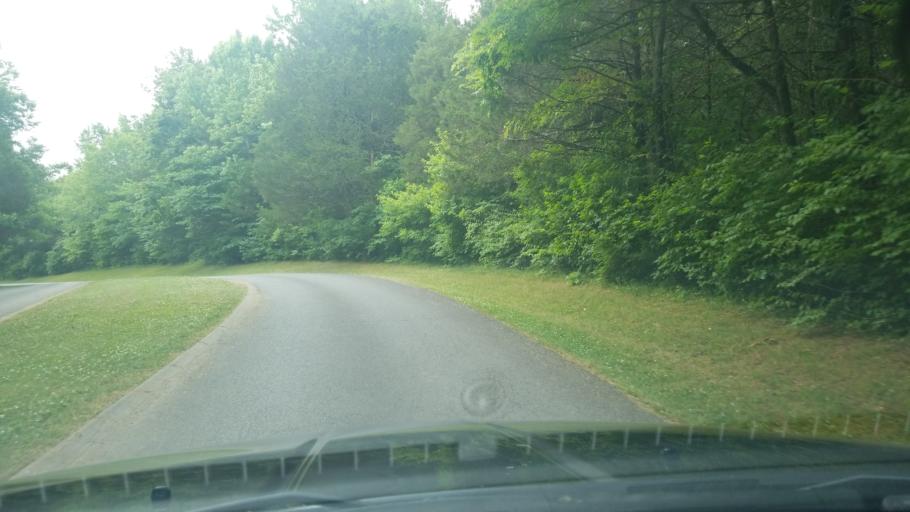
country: US
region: Tennessee
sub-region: Davidson County
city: Goodlettsville
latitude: 36.2695
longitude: -86.7504
